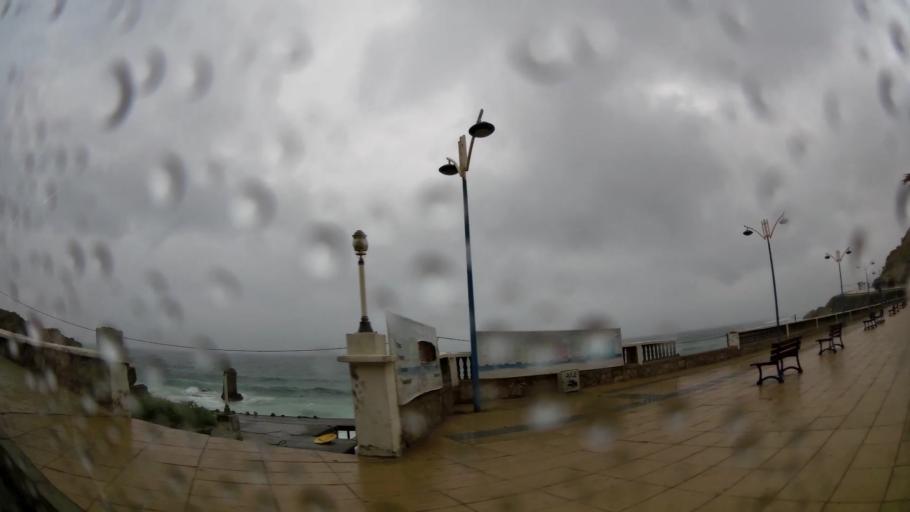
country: MA
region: Taza-Al Hoceima-Taounate
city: Tirhanimine
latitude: 35.2446
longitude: -3.9643
